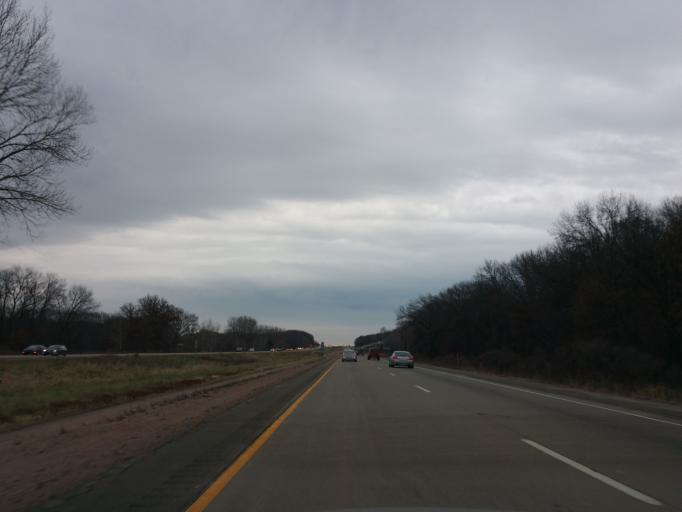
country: US
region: Wisconsin
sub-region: Columbia County
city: Portage
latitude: 43.5391
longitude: -89.6028
